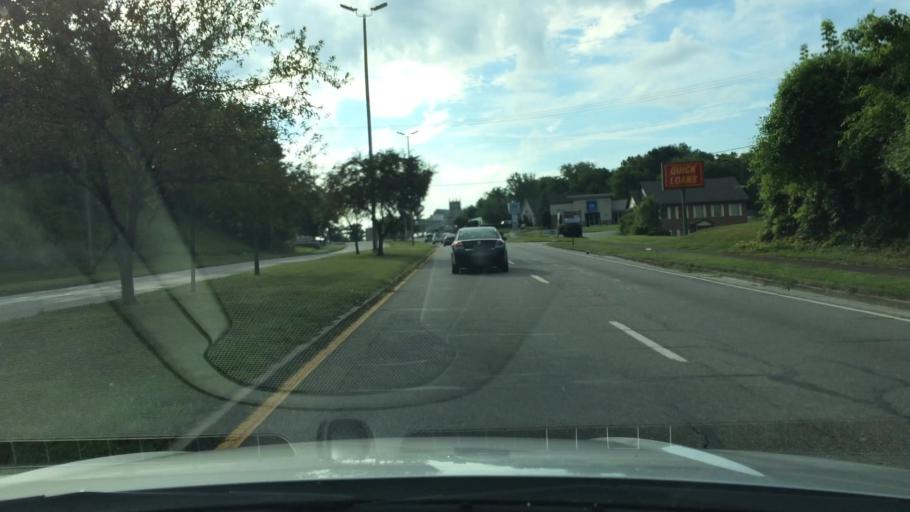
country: US
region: Tennessee
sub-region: Blount County
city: Maryville
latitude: 35.7516
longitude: -83.9836
